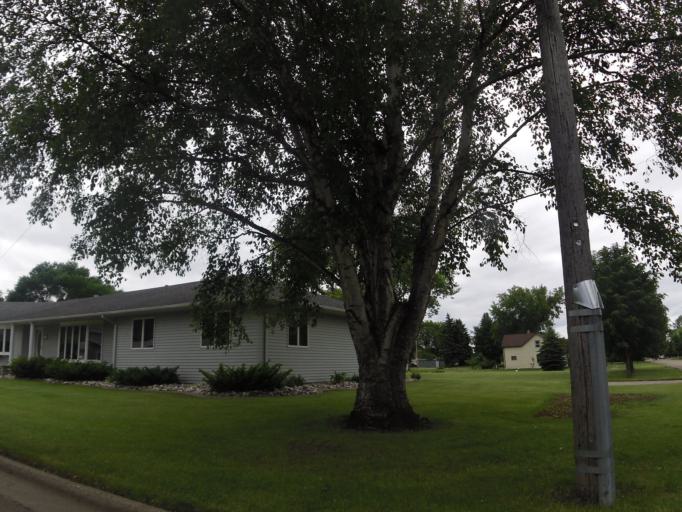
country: US
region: North Dakota
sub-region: Walsh County
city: Grafton
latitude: 48.6223
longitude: -97.4504
